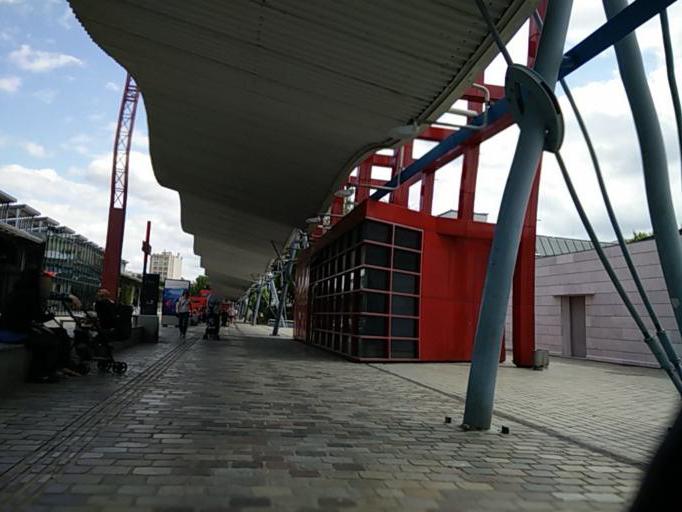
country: FR
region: Ile-de-France
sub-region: Departement de Seine-Saint-Denis
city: Le Pre-Saint-Gervais
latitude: 48.8909
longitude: 2.3900
